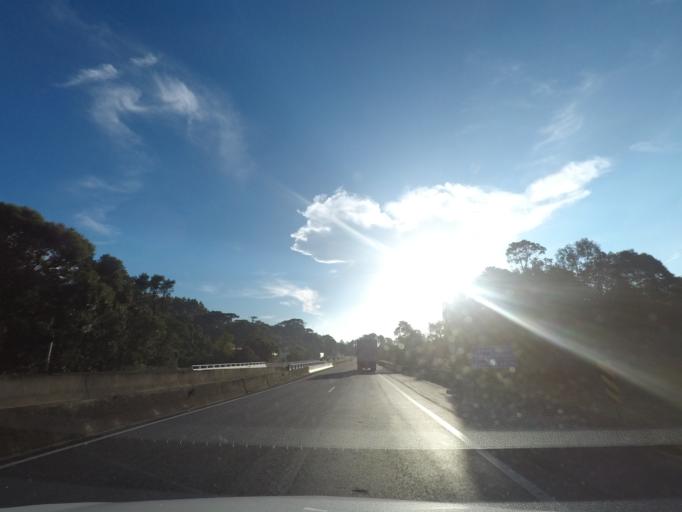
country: BR
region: Parana
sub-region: Campina Grande Do Sul
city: Campina Grande do Sul
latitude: -25.3034
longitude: -48.9585
